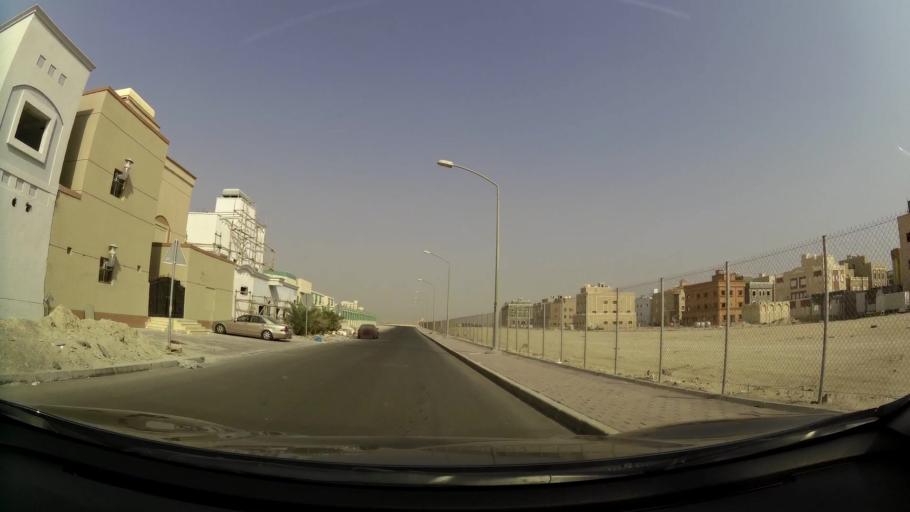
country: KW
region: Muhafazat al Jahra'
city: Al Jahra'
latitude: 29.3569
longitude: 47.7630
